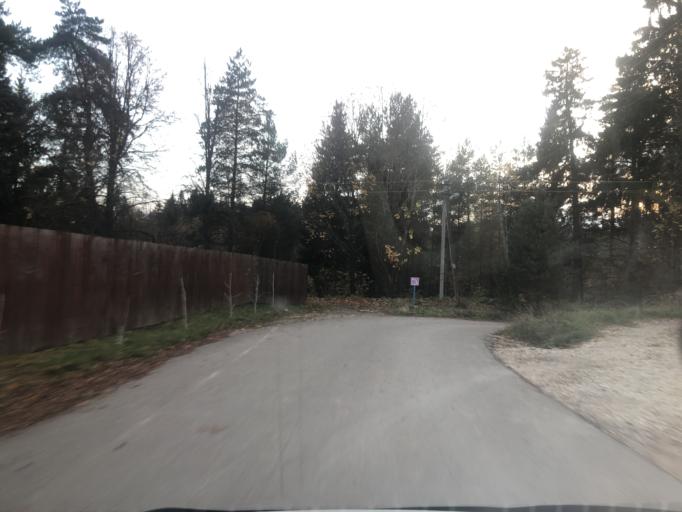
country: RU
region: Moskovskaya
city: Fryanovo
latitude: 56.1516
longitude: 38.3893
